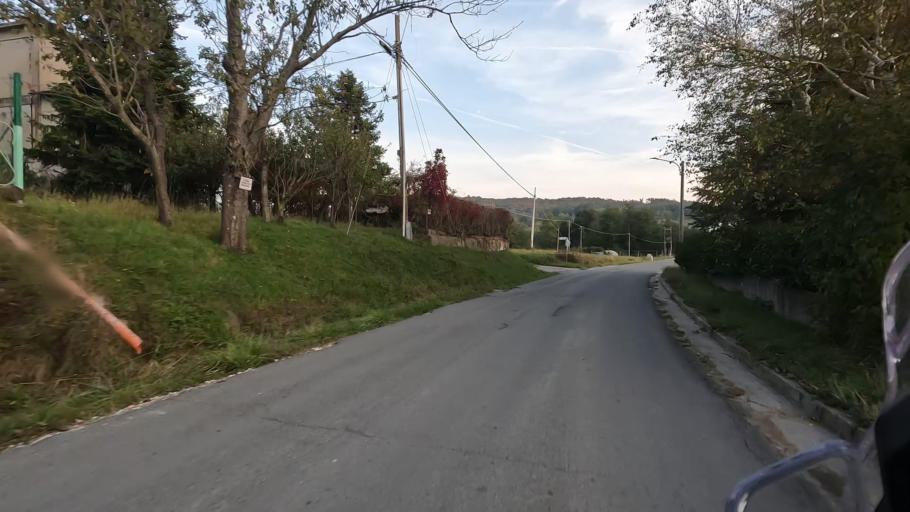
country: IT
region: Liguria
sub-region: Provincia di Savona
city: Mioglia
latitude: 44.4725
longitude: 8.4163
